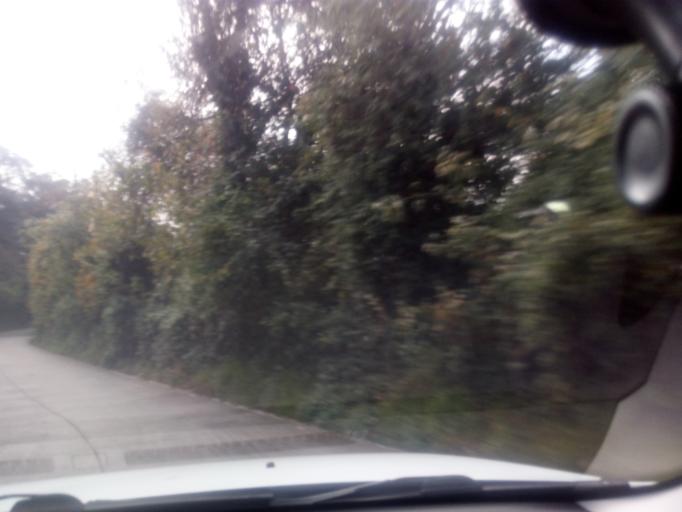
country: GT
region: Sacatepequez
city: San Bartolome Milpas Altas
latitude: 14.6001
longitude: -90.6790
